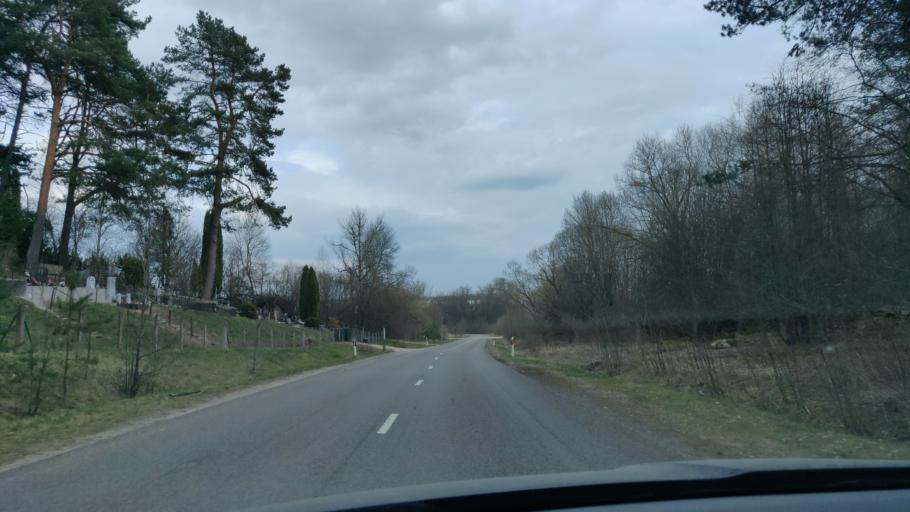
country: LT
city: Baltoji Voke
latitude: 54.6128
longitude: 25.1277
